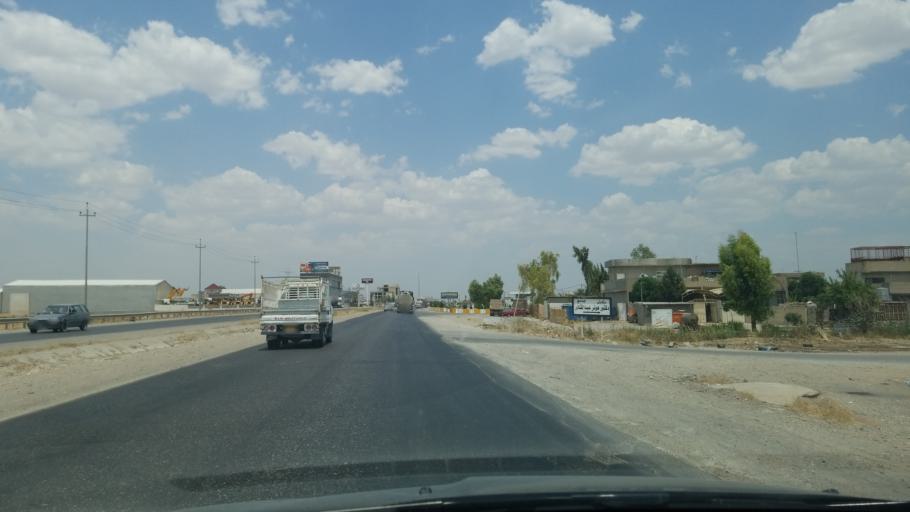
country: IQ
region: Arbil
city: Erbil
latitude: 36.0975
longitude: 44.0214
